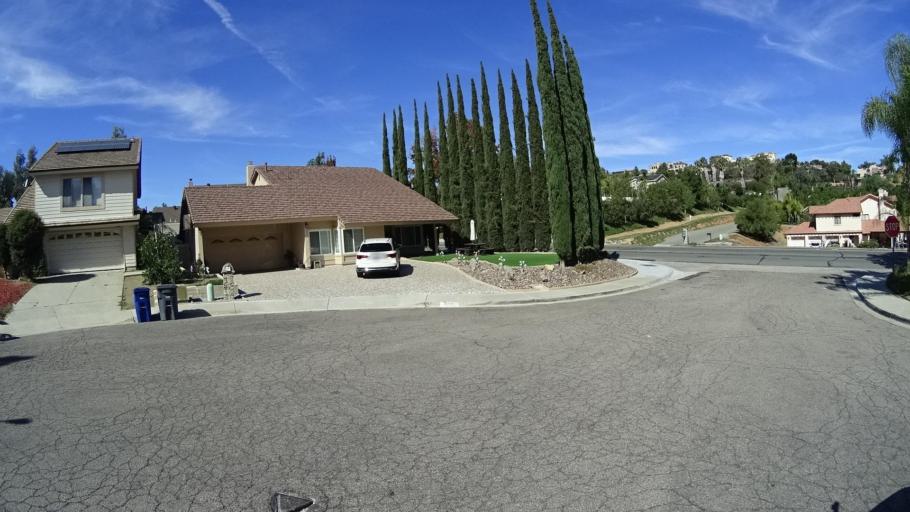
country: US
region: California
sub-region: San Diego County
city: Rancho San Diego
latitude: 32.7509
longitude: -116.9490
